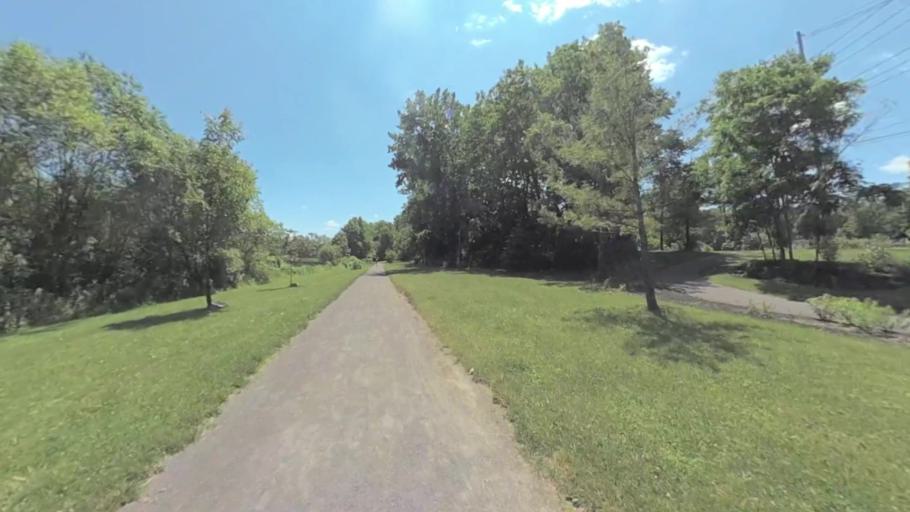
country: US
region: New York
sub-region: Monroe County
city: Fairport
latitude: 43.1000
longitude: -77.4366
